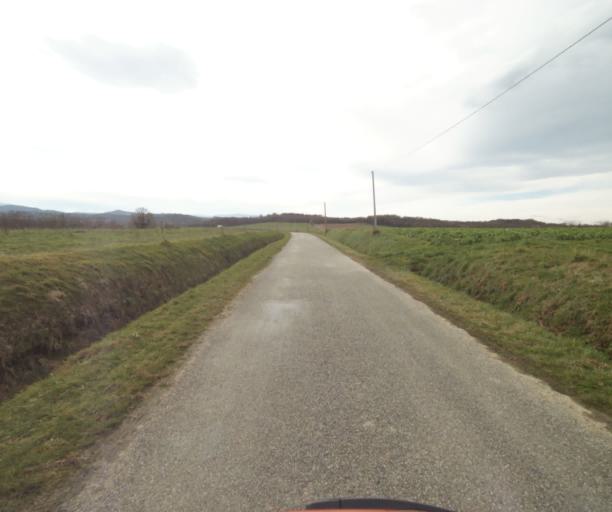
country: FR
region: Midi-Pyrenees
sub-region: Departement de l'Ariege
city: La Tour-du-Crieu
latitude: 43.0849
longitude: 1.7135
